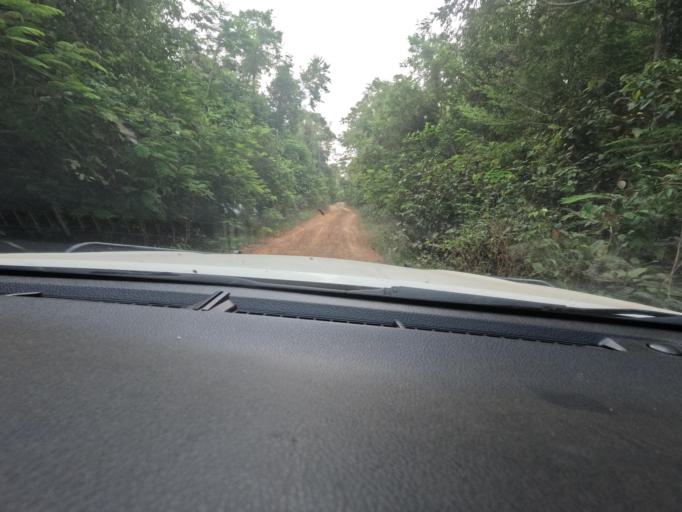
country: BR
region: Rondonia
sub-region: Porto Velho
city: Porto Velho
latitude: -8.6535
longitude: -63.1559
